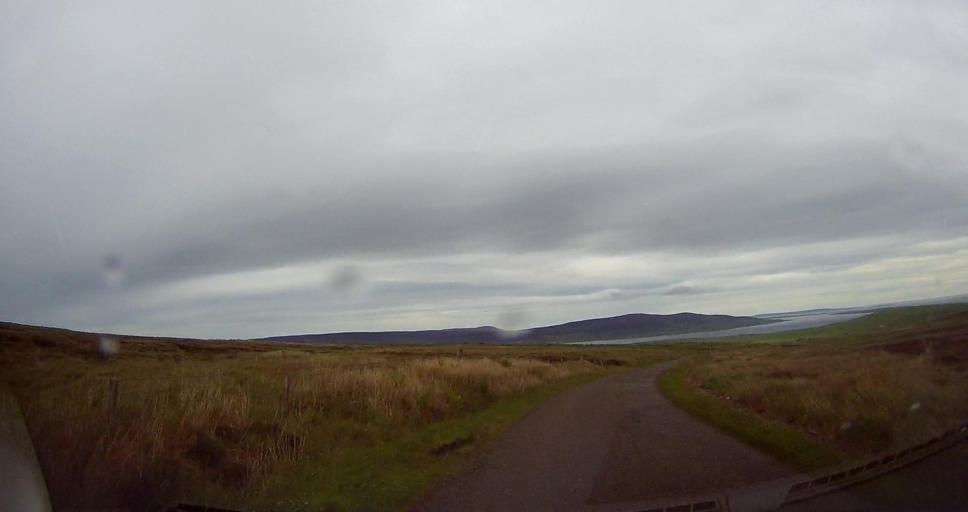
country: GB
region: Scotland
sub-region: Orkney Islands
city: Orkney
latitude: 59.1040
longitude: -3.1340
